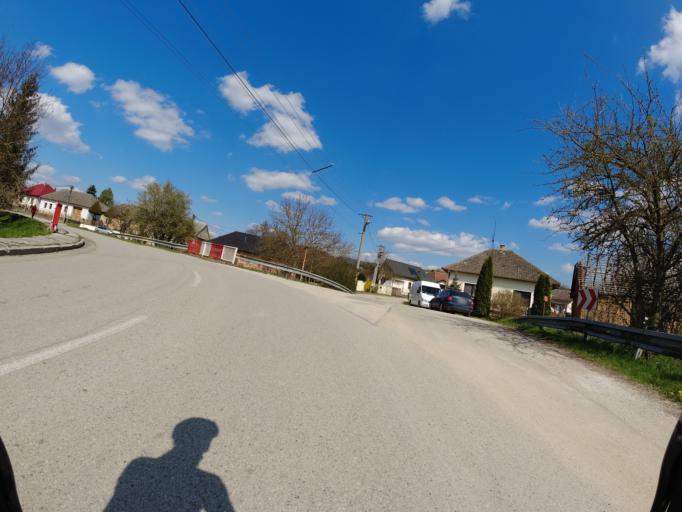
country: SK
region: Nitriansky
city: Stara Tura
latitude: 48.7381
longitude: 17.7249
